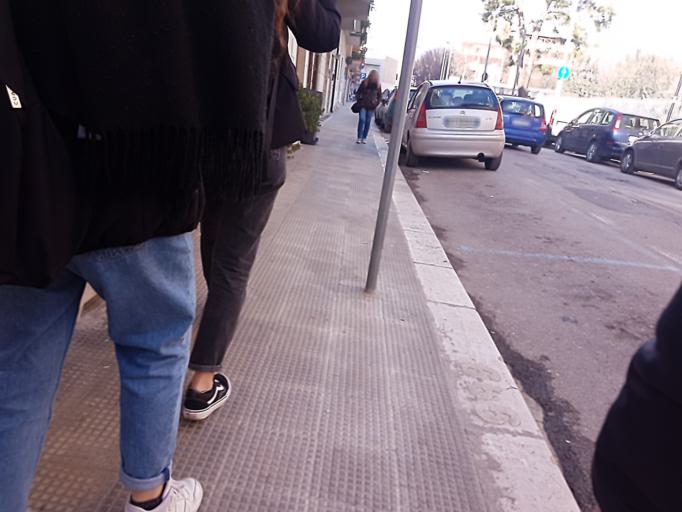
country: IT
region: Apulia
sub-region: Provincia di Barletta - Andria - Trani
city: Andria
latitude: 41.2316
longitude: 16.2966
